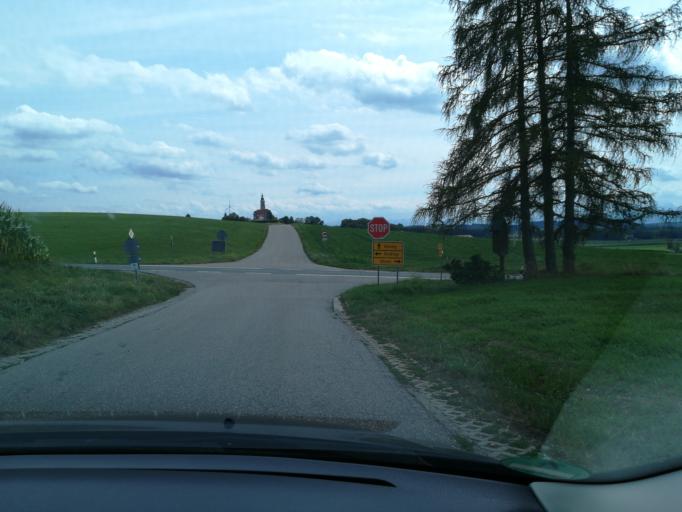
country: DE
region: Bavaria
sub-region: Upper Bavaria
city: Bruck
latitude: 48.0274
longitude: 11.9196
